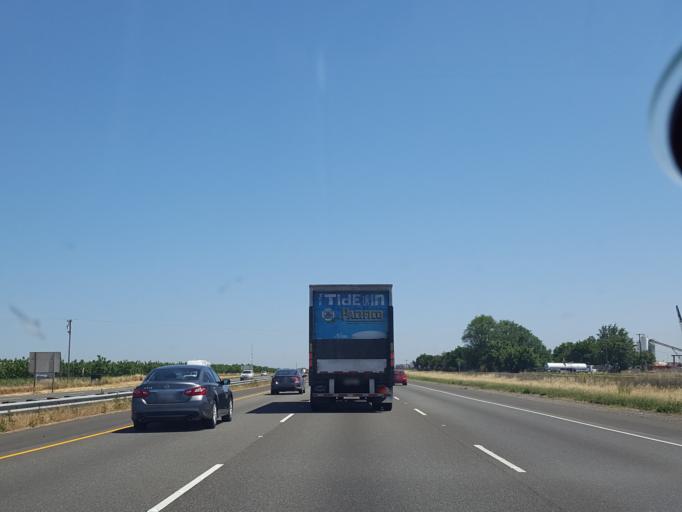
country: US
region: California
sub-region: Solano County
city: Dixon
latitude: 38.4946
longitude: -121.7970
